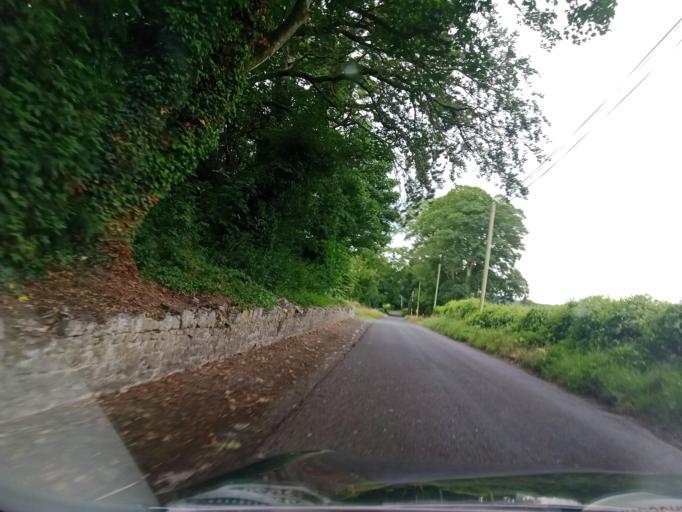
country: IE
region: Leinster
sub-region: Laois
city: Stradbally
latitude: 52.9894
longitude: -7.1749
